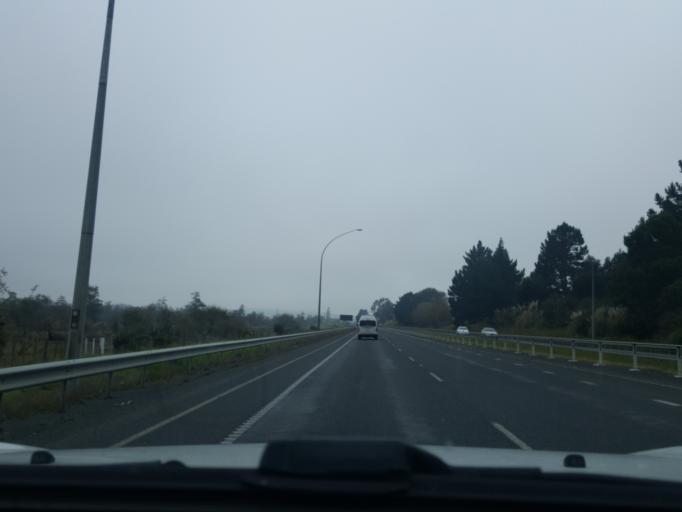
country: NZ
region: Waikato
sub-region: Waikato District
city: Te Kauwhata
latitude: -37.3228
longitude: 175.0662
